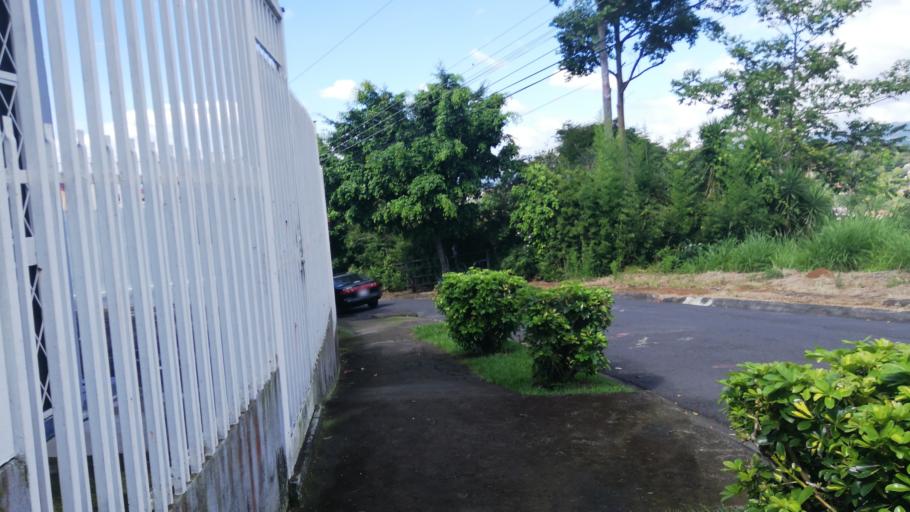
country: CR
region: Alajuela
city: San Juan
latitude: 10.0794
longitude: -84.3093
